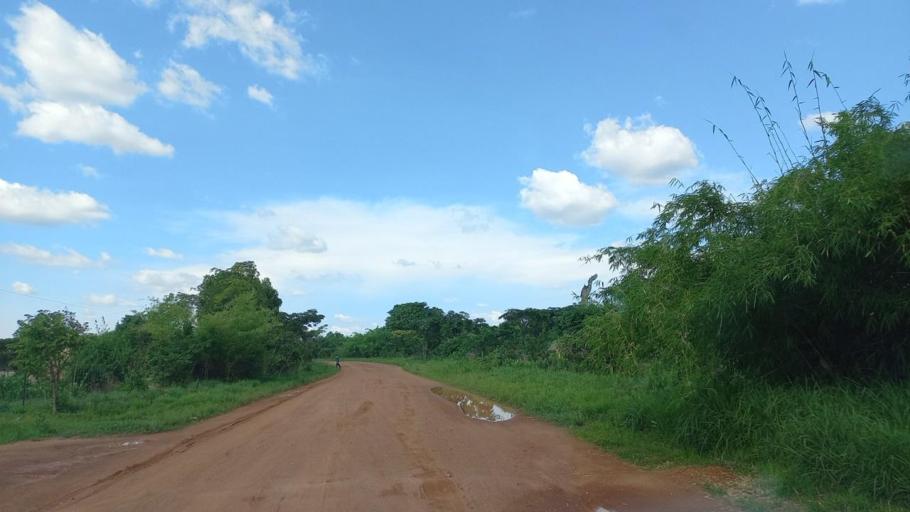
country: ZM
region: Copperbelt
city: Kitwe
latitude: -12.8533
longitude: 28.3893
